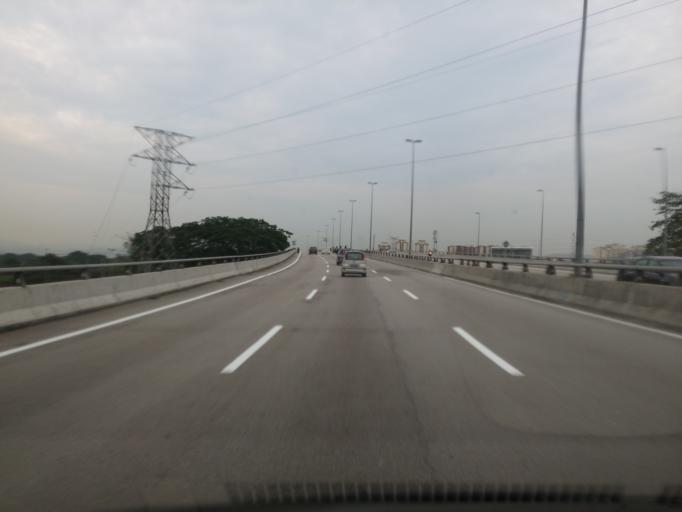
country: MY
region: Kuala Lumpur
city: Kuala Lumpur
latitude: 3.0986
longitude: 101.6997
